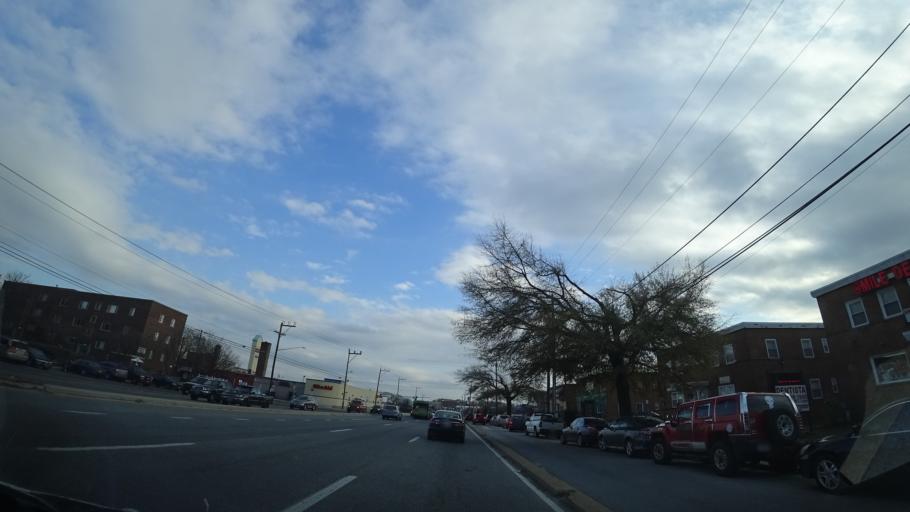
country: US
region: Maryland
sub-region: Prince George's County
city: Langley Park
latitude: 38.9918
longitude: -76.9907
